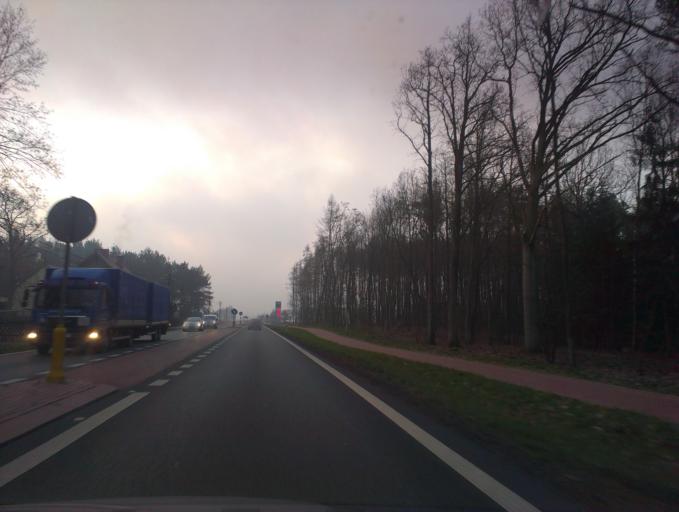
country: PL
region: Greater Poland Voivodeship
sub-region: Powiat chodzieski
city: Chodziez
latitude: 52.9650
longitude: 16.9331
